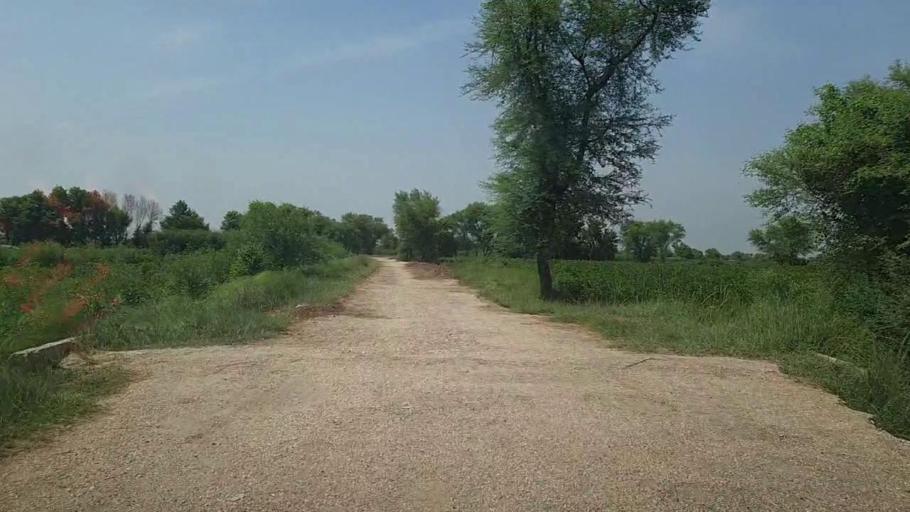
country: PK
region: Sindh
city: Ubauro
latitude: 28.1743
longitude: 69.8151
